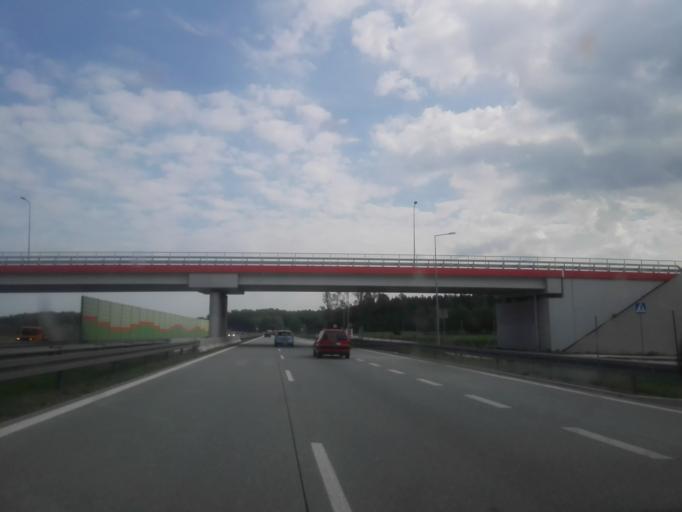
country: PL
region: Lodz Voivodeship
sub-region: Powiat tomaszowski
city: Czerniewice
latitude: 51.6934
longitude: 20.2119
